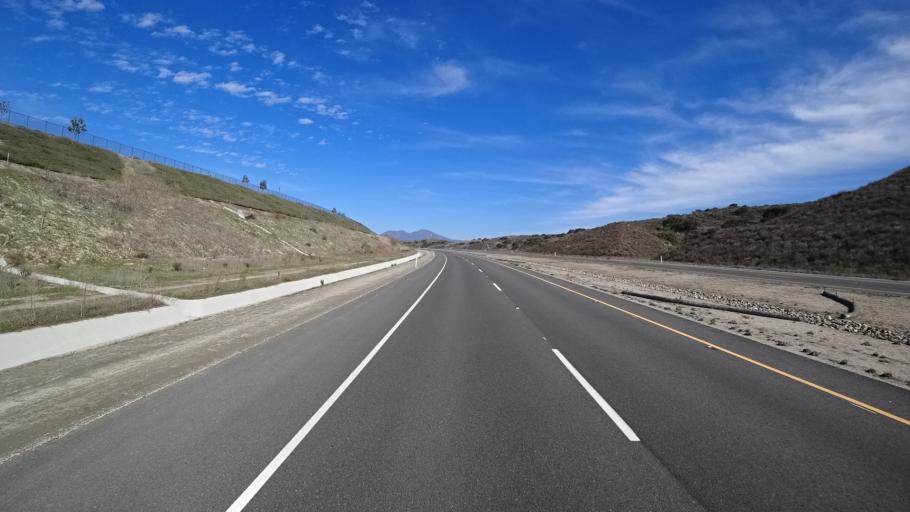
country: US
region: California
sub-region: Orange County
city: Ladera Ranch
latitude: 33.5340
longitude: -117.5958
